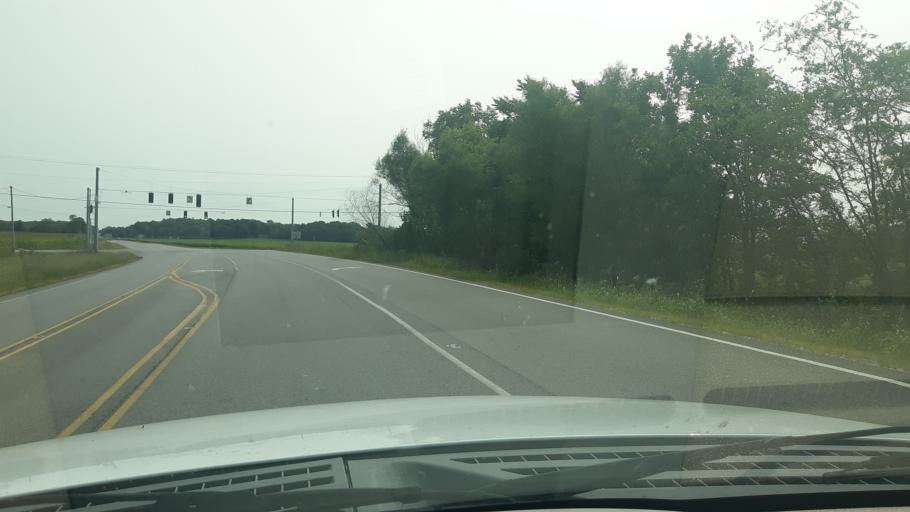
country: US
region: Indiana
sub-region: Gibson County
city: Owensville
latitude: 38.3561
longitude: -87.6887
